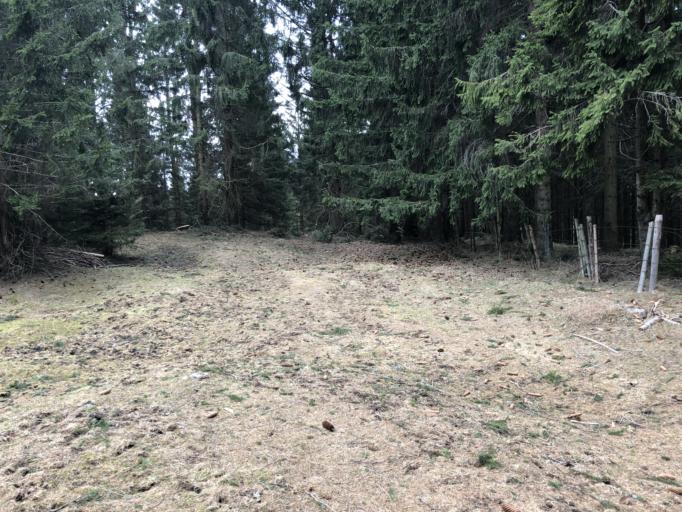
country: AT
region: Styria
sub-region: Politischer Bezirk Weiz
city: Stenzengreith
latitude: 47.2246
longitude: 15.5059
